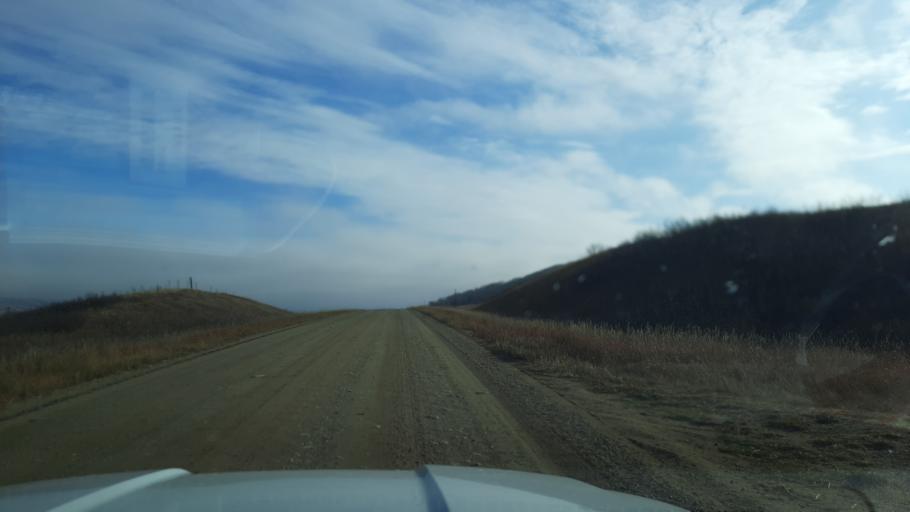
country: CA
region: Saskatchewan
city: Pilot Butte
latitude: 50.7841
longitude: -104.2255
